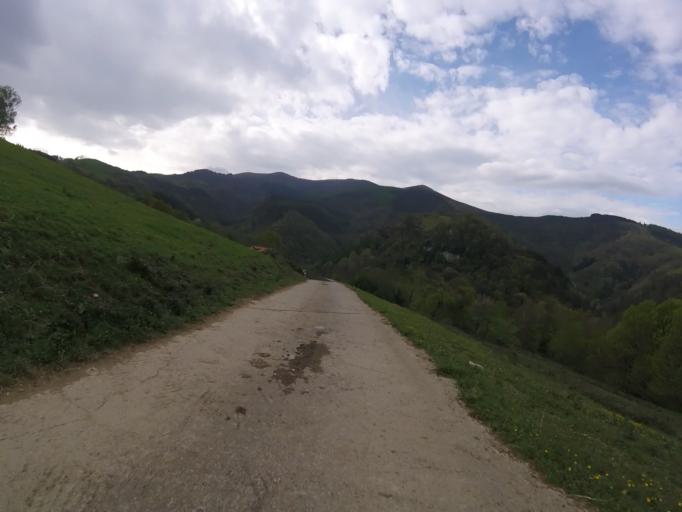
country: ES
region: Basque Country
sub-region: Provincia de Guipuzcoa
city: Aya
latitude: 43.2092
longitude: -2.1767
